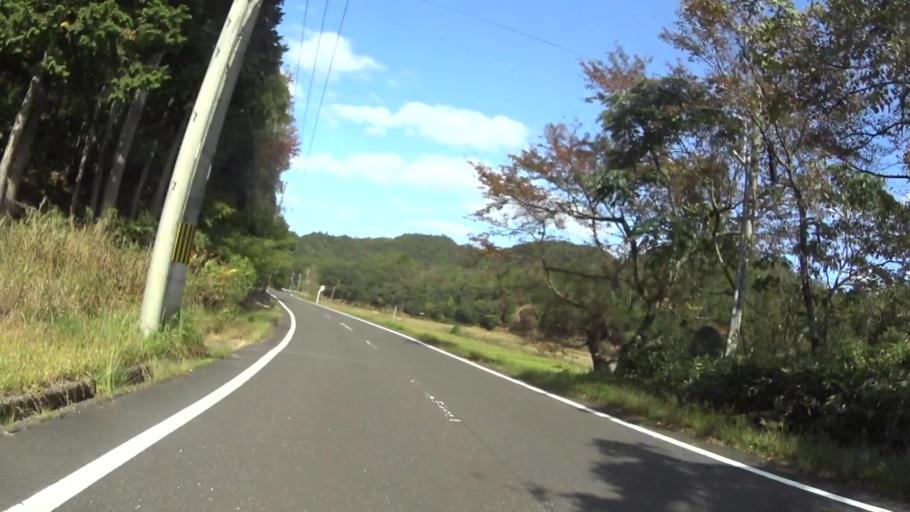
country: JP
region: Hyogo
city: Toyooka
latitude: 35.5560
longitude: 134.9777
